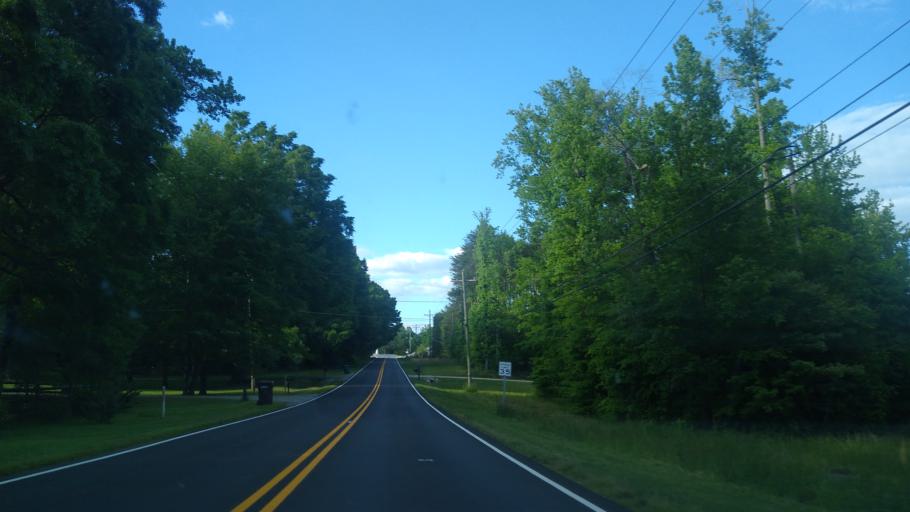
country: US
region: North Carolina
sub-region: Guilford County
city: McLeansville
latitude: 36.1548
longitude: -79.7383
